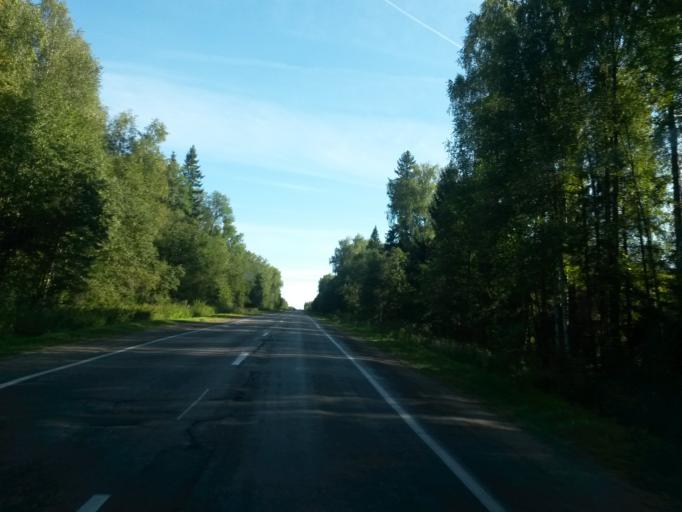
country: RU
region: Jaroslavl
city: Gavrilov-Yam
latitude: 57.4202
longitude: 39.9196
